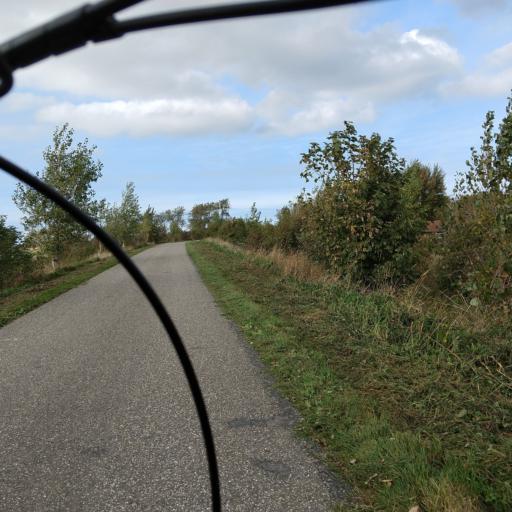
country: NL
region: Zeeland
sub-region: Schouwen-Duiveland
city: Scharendijke
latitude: 51.7007
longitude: 3.9329
